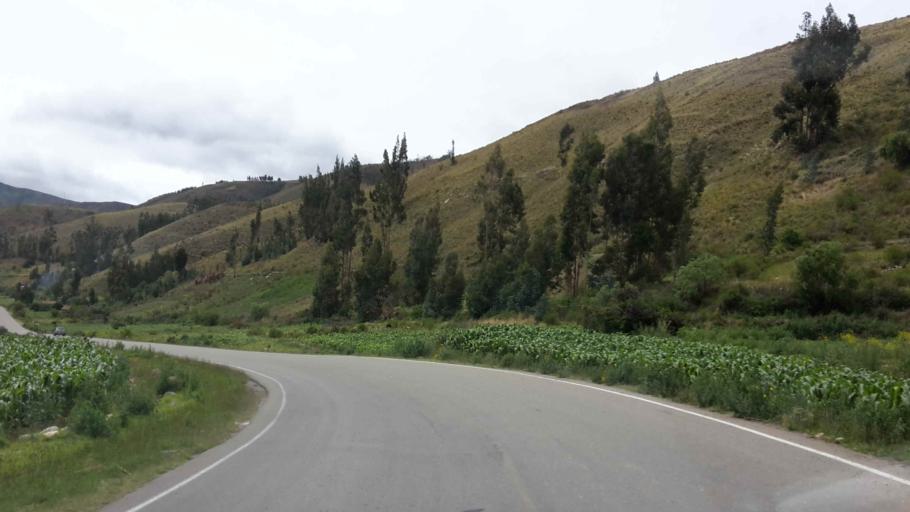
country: BO
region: Cochabamba
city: Colomi
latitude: -17.4111
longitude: -65.7746
